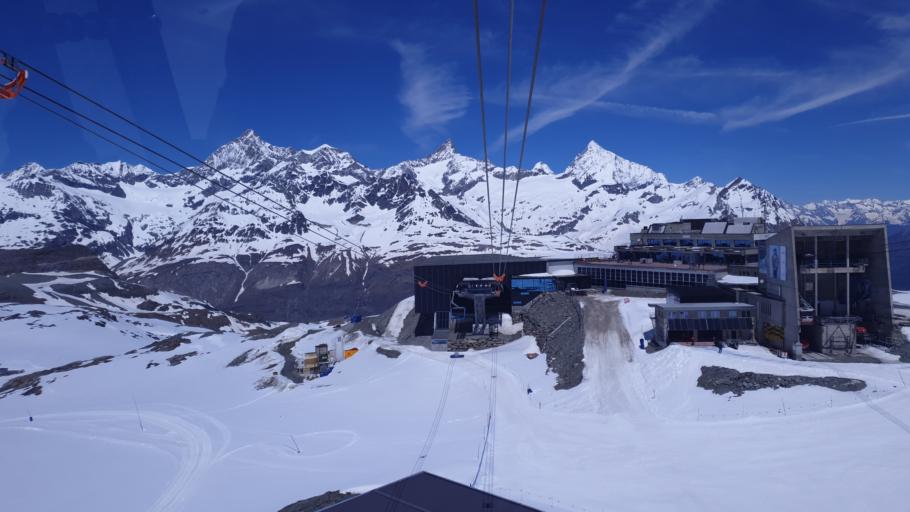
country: CH
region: Valais
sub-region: Visp District
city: Zermatt
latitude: 45.9696
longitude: 7.7219
